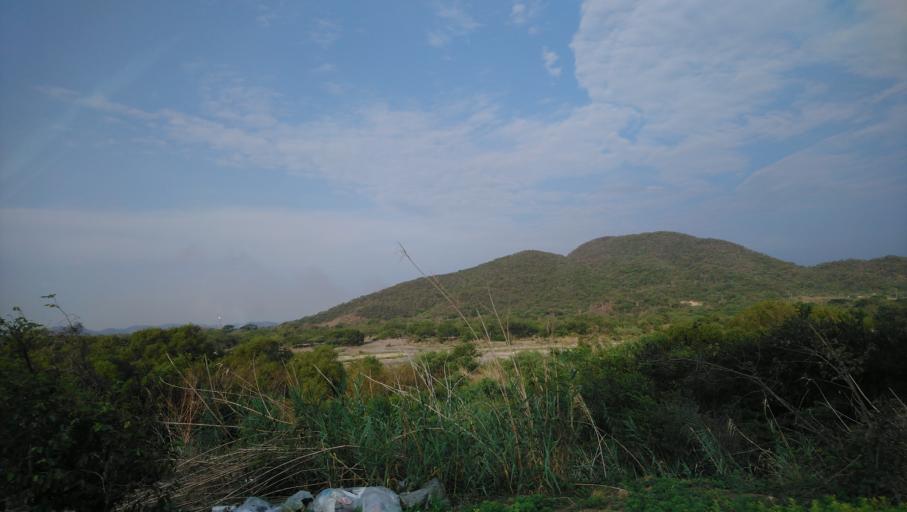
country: MX
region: Oaxaca
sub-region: Santo Domingo Tehuantepec
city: La Noria
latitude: 16.2368
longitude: -95.1536
